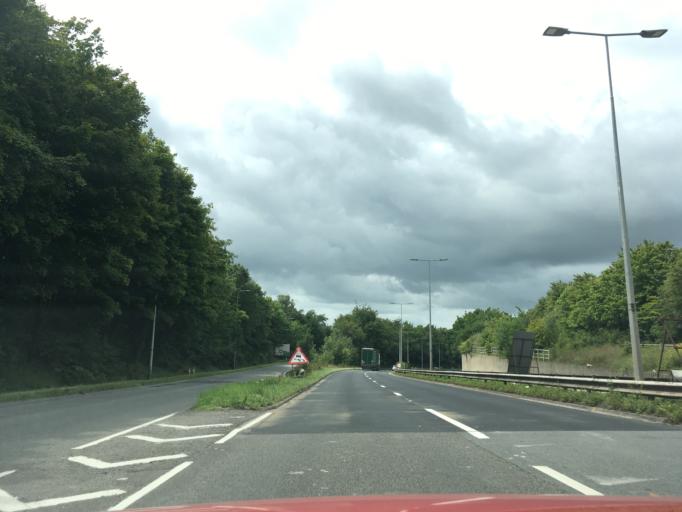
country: GB
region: Wales
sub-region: Cardiff
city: Radyr
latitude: 51.4654
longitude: -3.2655
